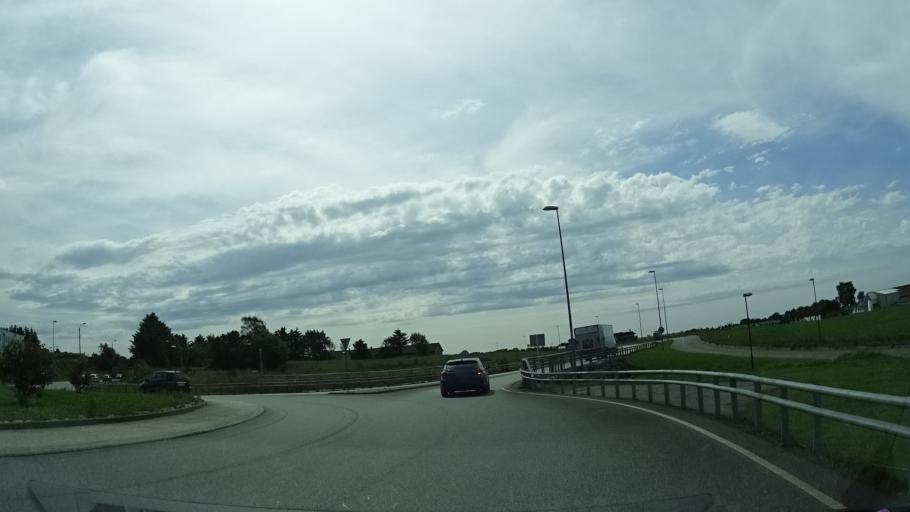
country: NO
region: Rogaland
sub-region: Randaberg
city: Randaberg
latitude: 58.9951
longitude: 5.6506
